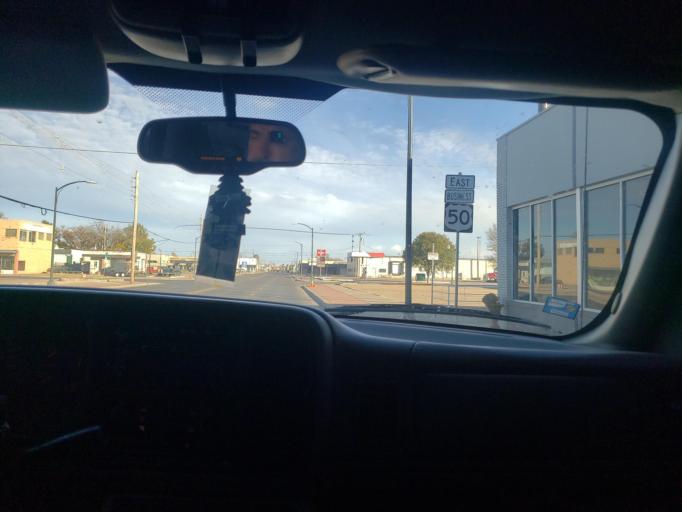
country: US
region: Kansas
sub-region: Finney County
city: Garden City
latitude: 37.9657
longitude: -100.8734
